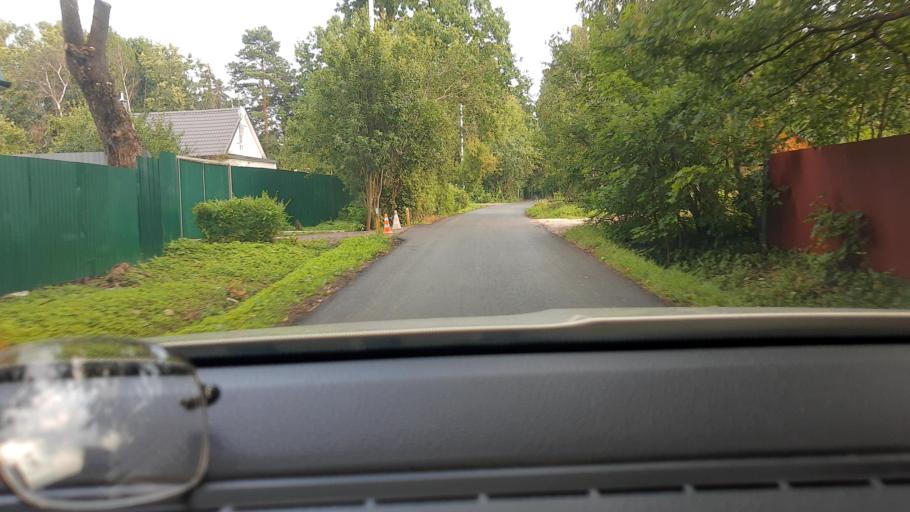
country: RU
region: Moskovskaya
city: Kokoshkino
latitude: 55.5949
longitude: 37.1617
